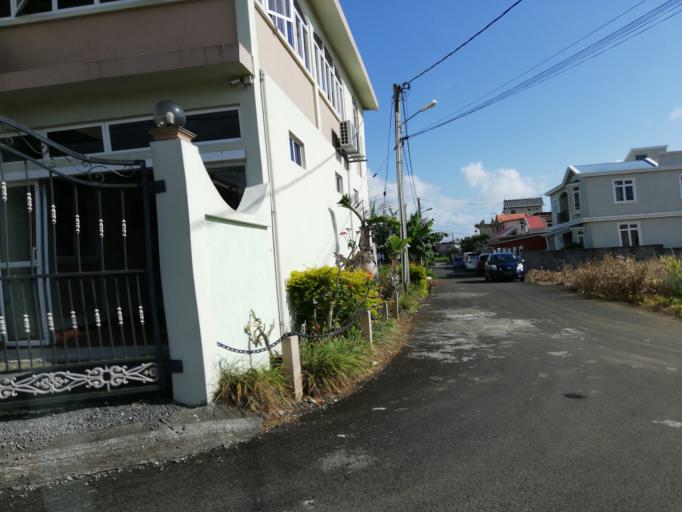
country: MU
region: Moka
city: Verdun
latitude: -20.2213
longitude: 57.5465
